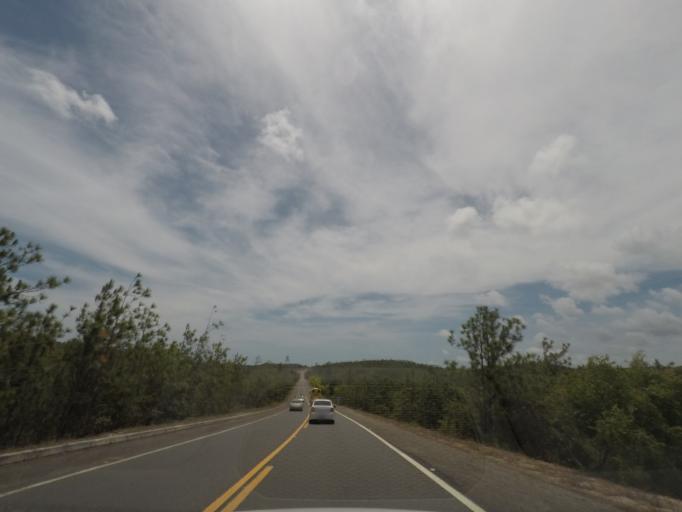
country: BR
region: Bahia
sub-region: Conde
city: Conde
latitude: -11.9836
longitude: -37.6772
